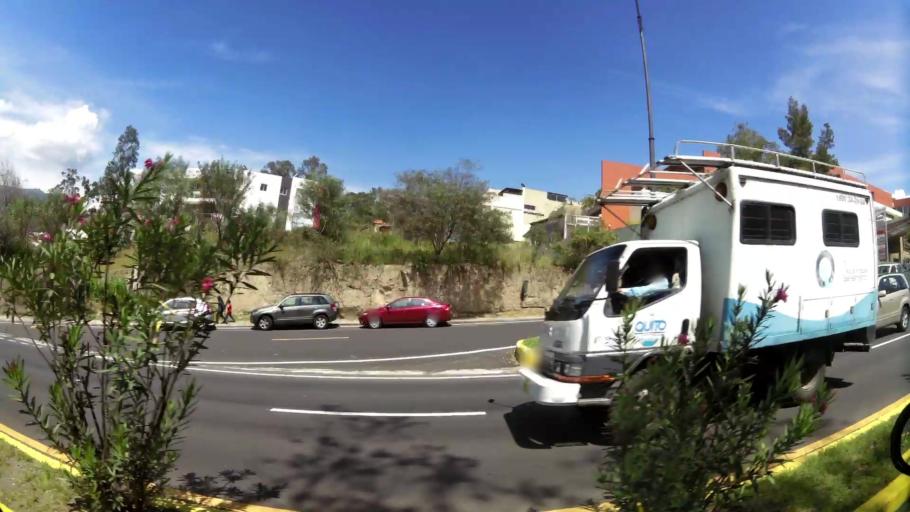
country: EC
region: Pichincha
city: Quito
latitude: -0.2044
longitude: -78.4364
